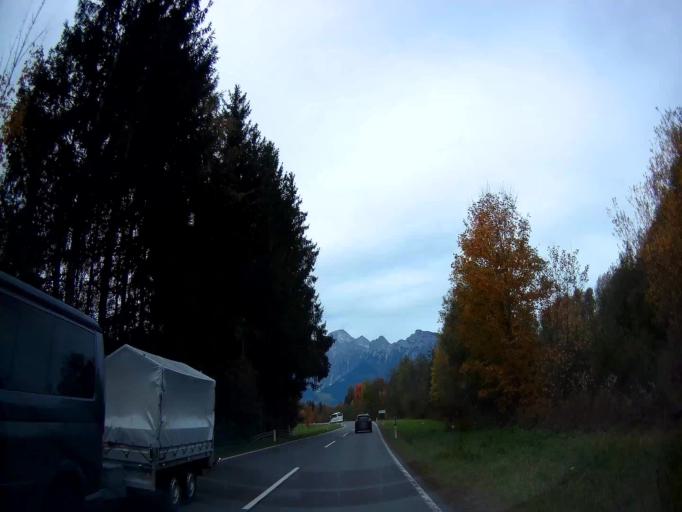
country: AT
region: Salzburg
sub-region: Politischer Bezirk Zell am See
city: Saalfelden am Steinernen Meer
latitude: 47.4156
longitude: 12.8650
